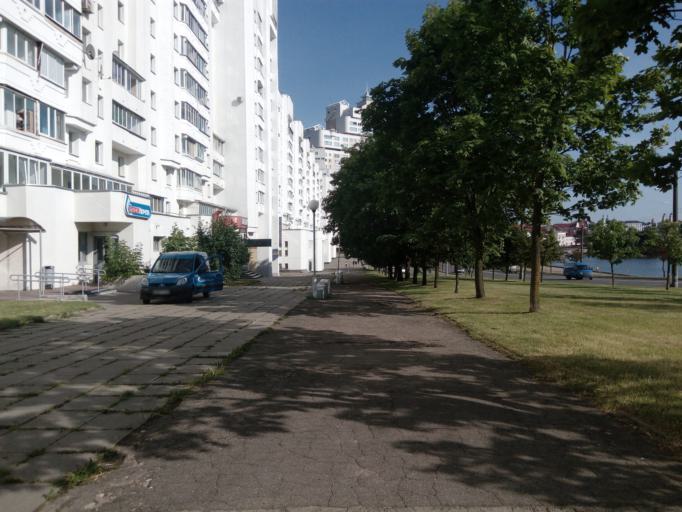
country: BY
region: Minsk
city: Minsk
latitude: 53.9135
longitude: 27.5545
